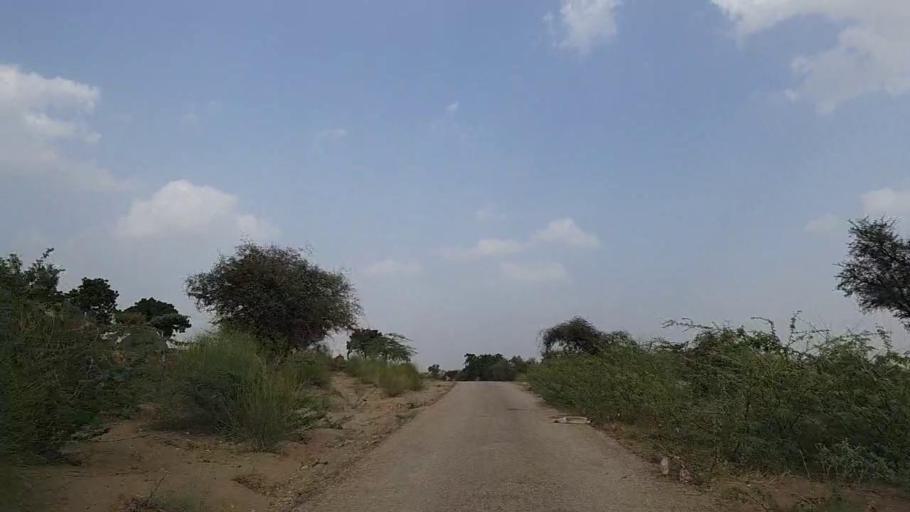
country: PK
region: Sindh
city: Islamkot
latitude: 24.7687
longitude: 70.1779
